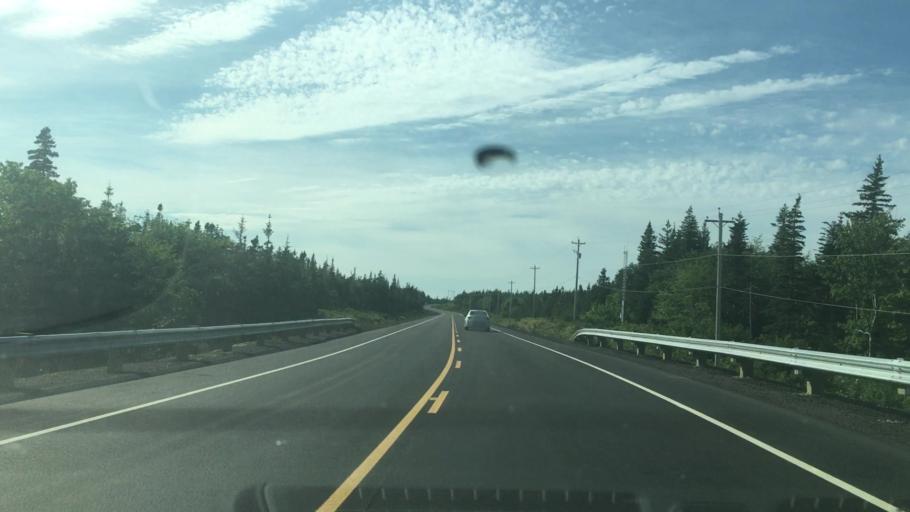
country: CA
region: Nova Scotia
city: Sydney Mines
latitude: 46.8417
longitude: -60.3938
